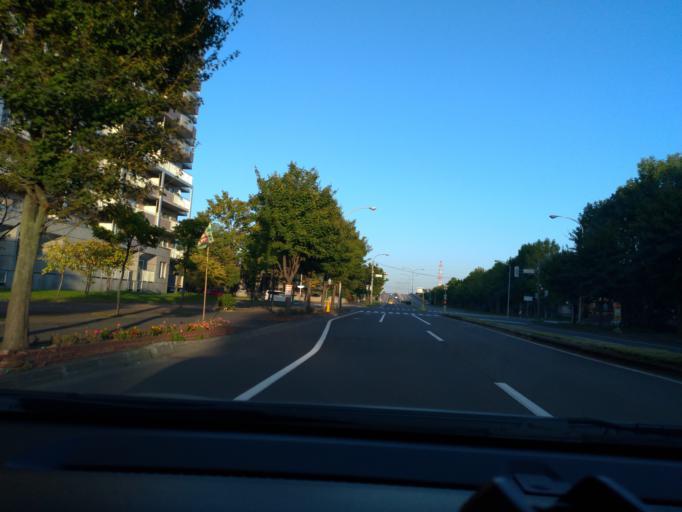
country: JP
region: Hokkaido
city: Ishikari
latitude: 43.1578
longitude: 141.4028
